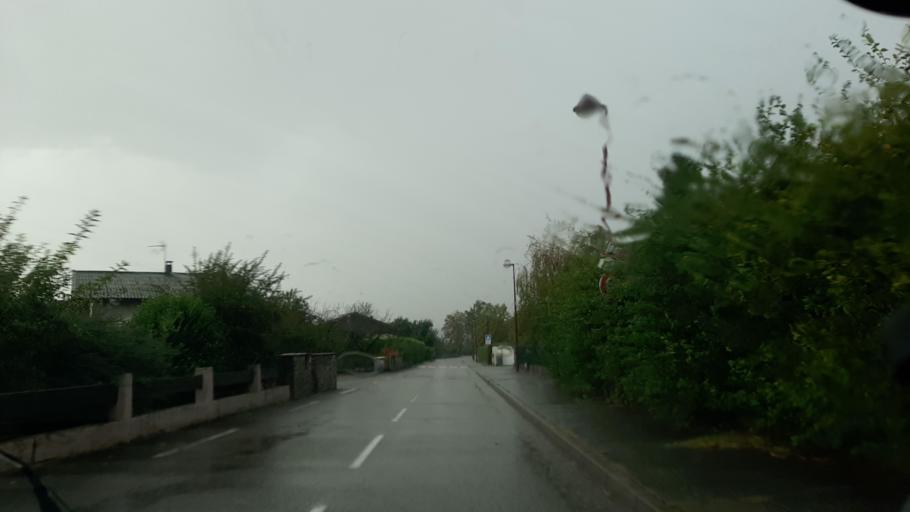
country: FR
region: Rhone-Alpes
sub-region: Departement de la Savoie
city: Gilly-sur-Isere
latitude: 45.6619
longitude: 6.3566
